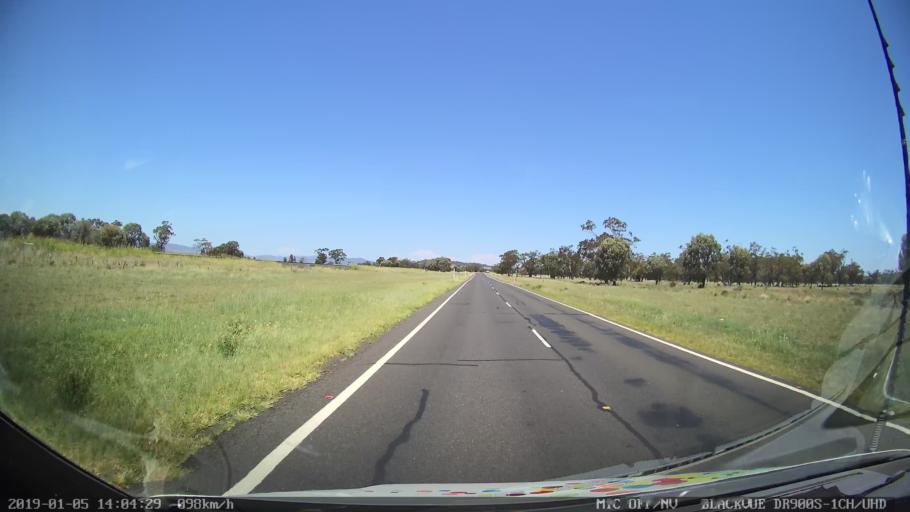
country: AU
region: New South Wales
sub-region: Gunnedah
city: Gunnedah
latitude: -31.2004
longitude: 150.3644
